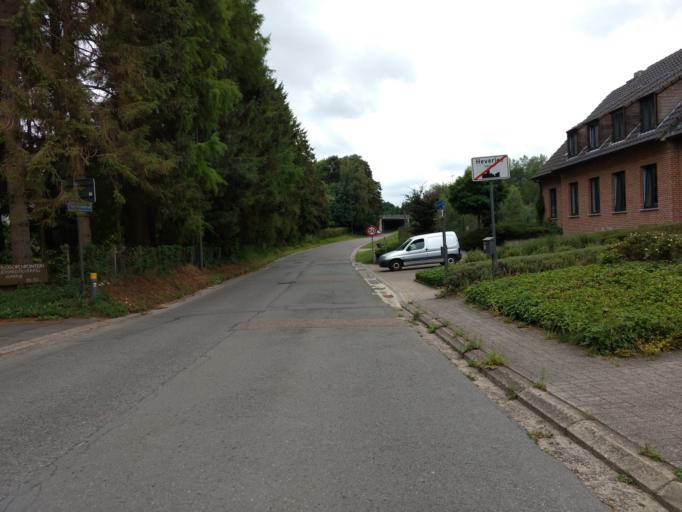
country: BE
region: Flanders
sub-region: Provincie Vlaams-Brabant
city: Oud-Heverlee
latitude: 50.8518
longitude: 4.6726
